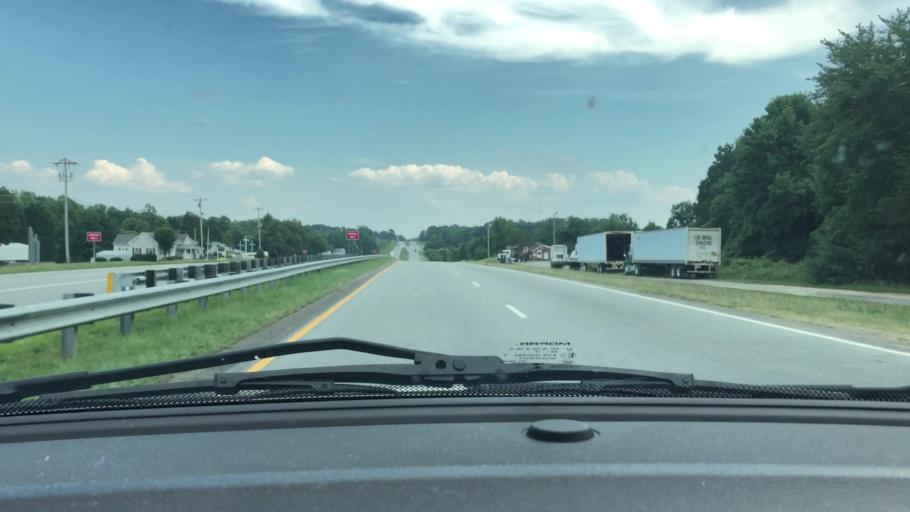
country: US
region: North Carolina
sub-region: Rockingham County
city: Madison
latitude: 36.3258
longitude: -79.9464
